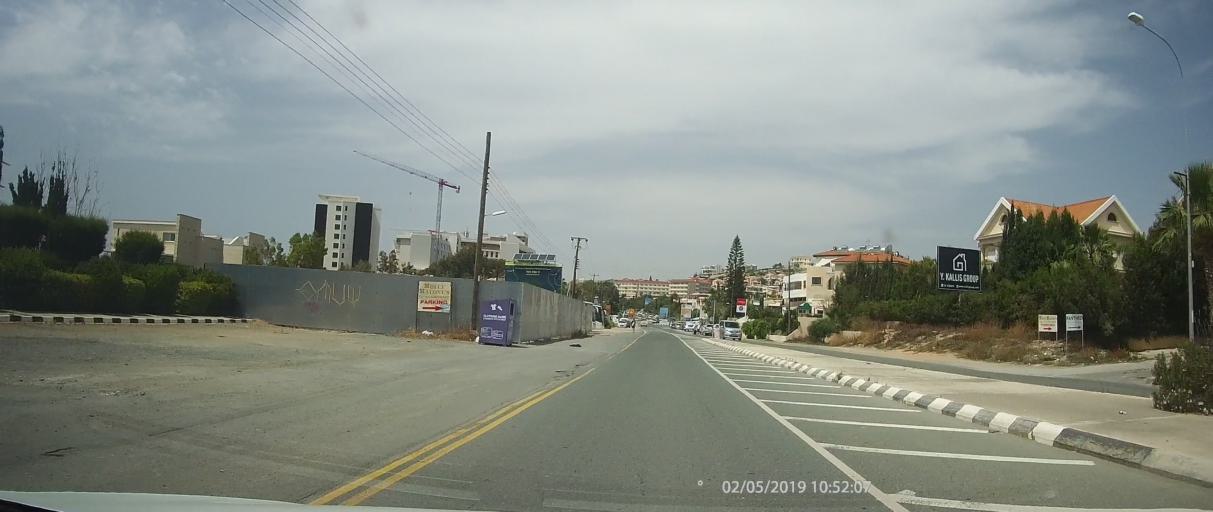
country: CY
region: Larnaka
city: Agios Tychon
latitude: 34.7145
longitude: 33.1592
